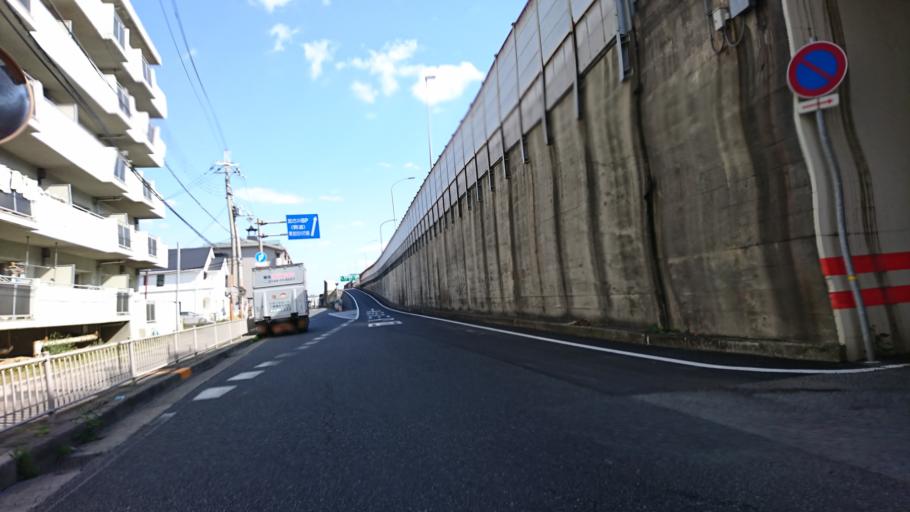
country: JP
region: Hyogo
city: Kakogawacho-honmachi
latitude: 34.7697
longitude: 134.8461
